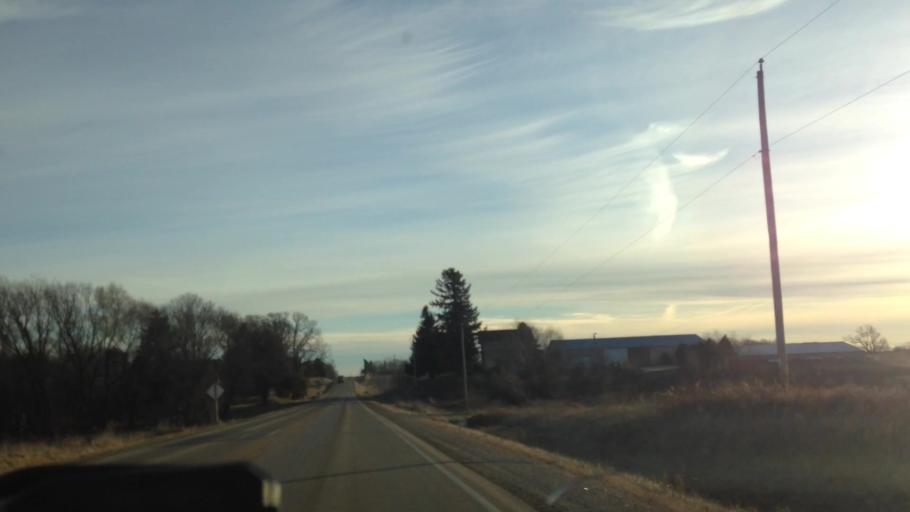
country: US
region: Wisconsin
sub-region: Dodge County
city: Theresa
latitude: 43.5366
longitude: -88.4781
